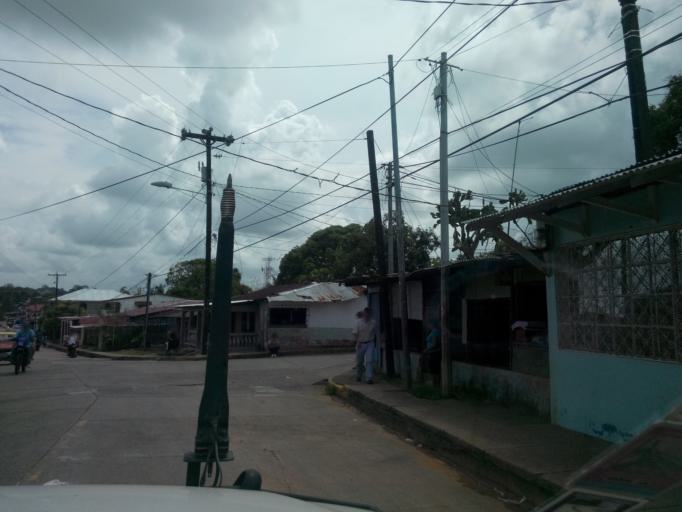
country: NI
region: Atlantico Sur
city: Bluefields
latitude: 12.0078
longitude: -83.7649
